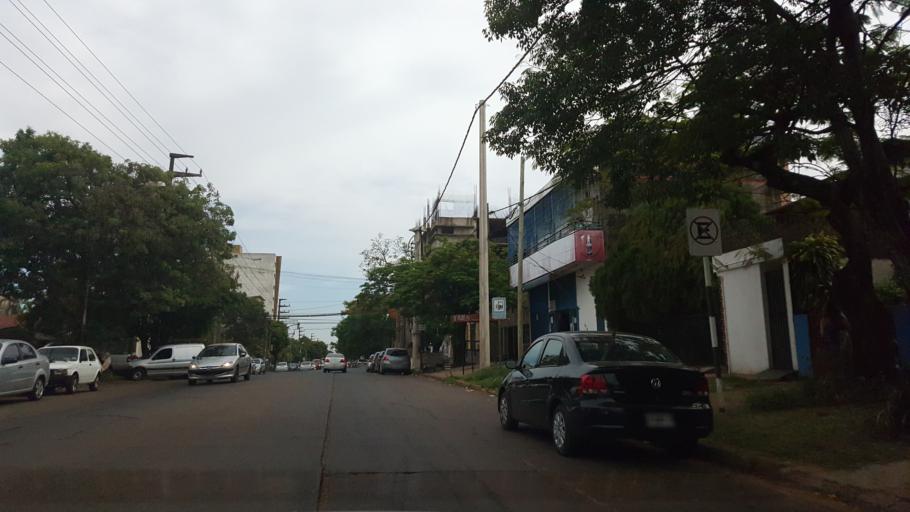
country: AR
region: Misiones
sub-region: Departamento de Capital
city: Posadas
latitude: -27.3672
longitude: -55.9089
